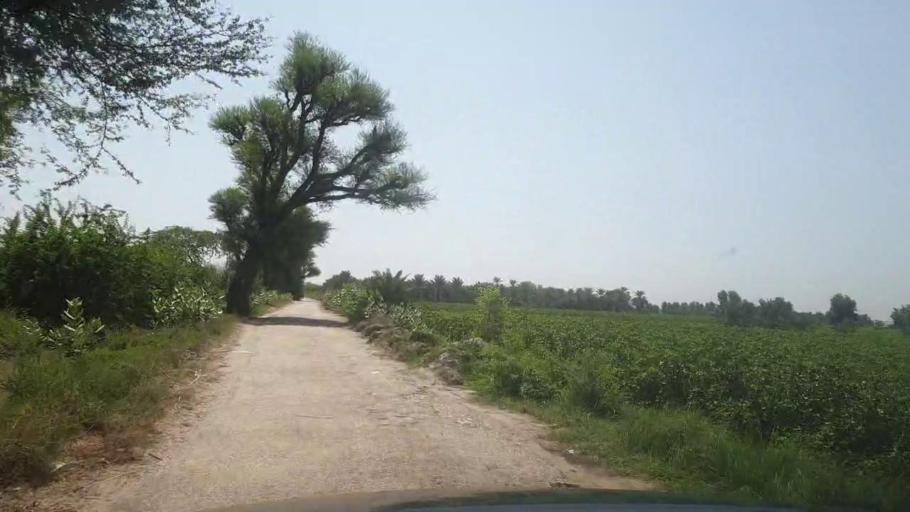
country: PK
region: Sindh
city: Khairpur
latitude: 27.3663
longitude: 69.0217
